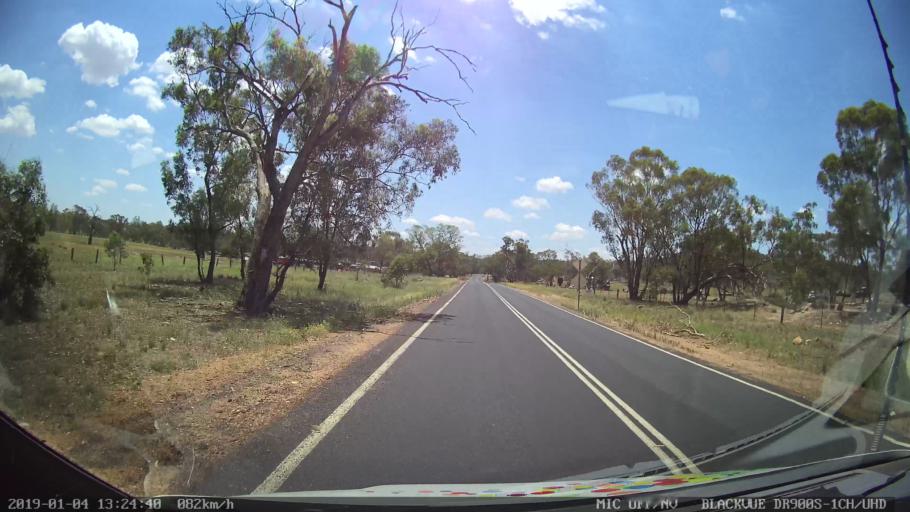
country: AU
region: New South Wales
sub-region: Parkes
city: Peak Hill
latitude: -32.7027
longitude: 148.5533
